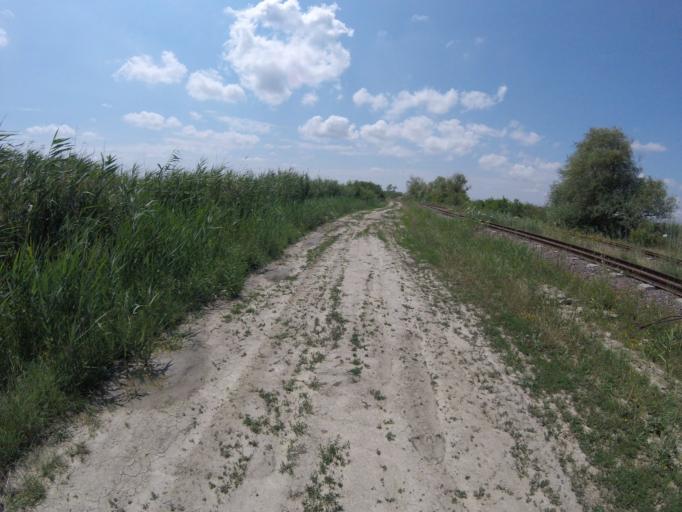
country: HU
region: Hajdu-Bihar
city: Hortobagy
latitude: 47.6466
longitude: 21.0882
